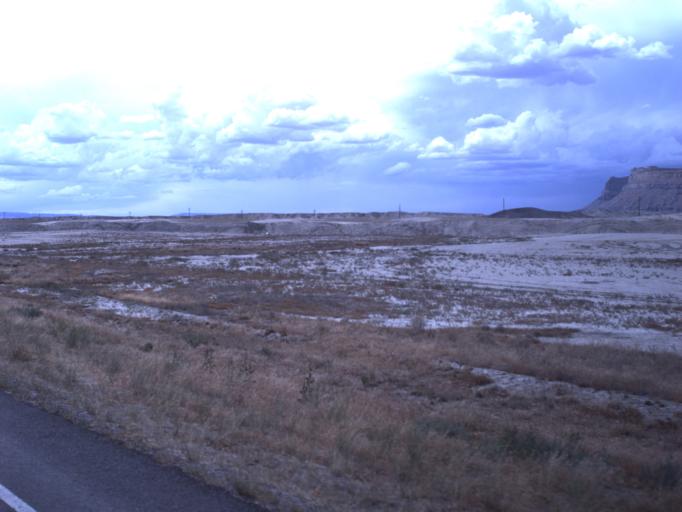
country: US
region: Utah
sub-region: Carbon County
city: East Carbon City
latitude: 38.9955
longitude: -110.1767
